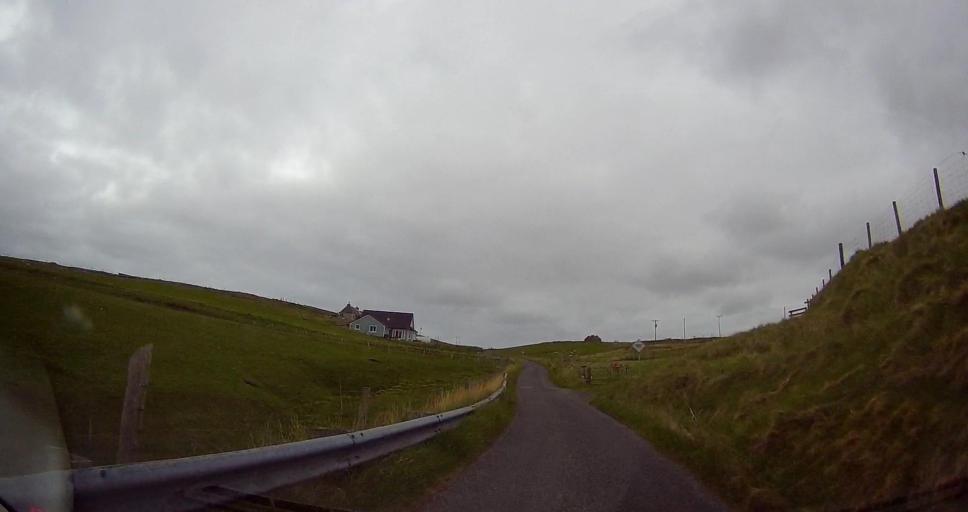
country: GB
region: Scotland
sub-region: Shetland Islands
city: Shetland
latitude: 60.8021
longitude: -0.8773
